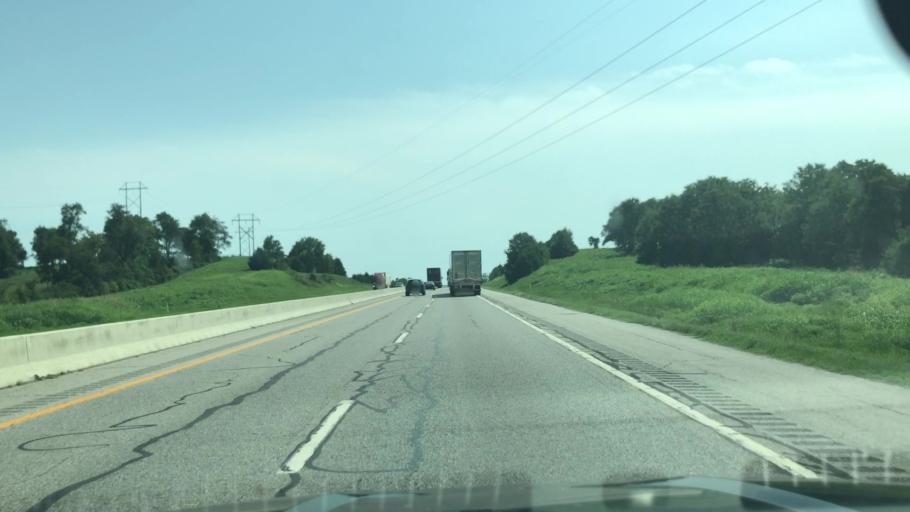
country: US
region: Oklahoma
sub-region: Ottawa County
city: Miami
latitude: 36.8365
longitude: -94.8636
